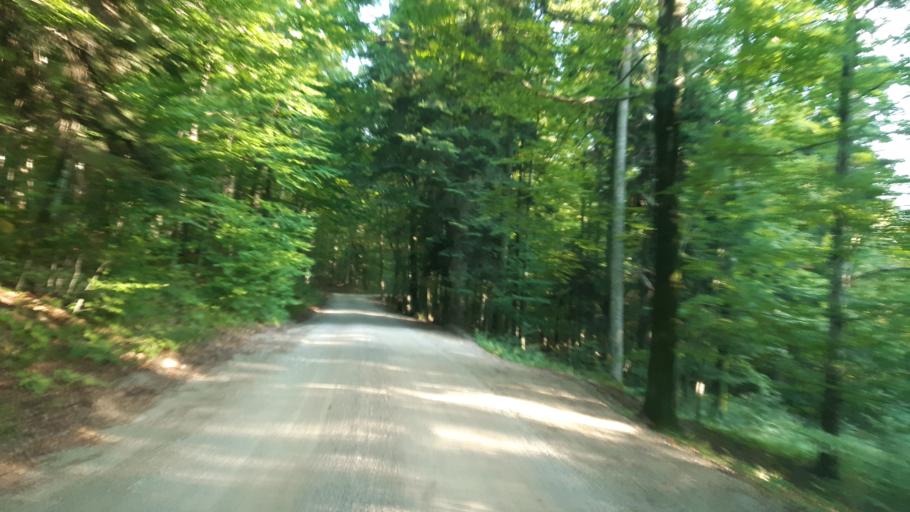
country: SI
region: Kocevje
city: Kocevje
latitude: 45.6744
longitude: 14.9734
